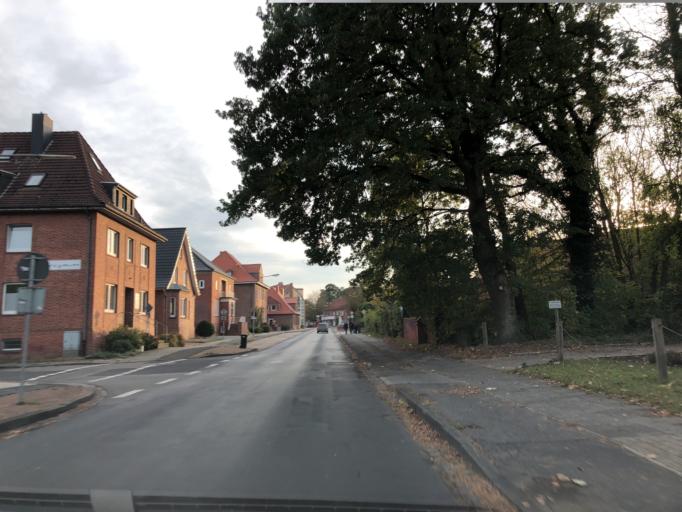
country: DE
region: Lower Saxony
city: Lehe
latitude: 53.0547
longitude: 7.3344
